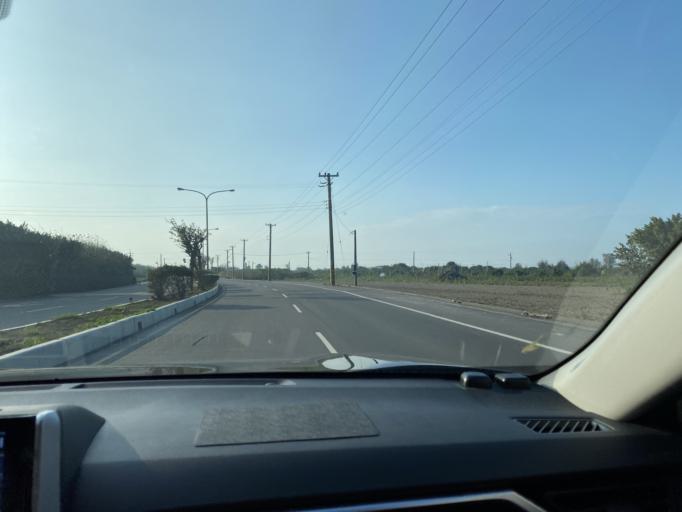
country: TW
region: Taiwan
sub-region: Changhua
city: Chang-hua
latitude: 23.9613
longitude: 120.3585
